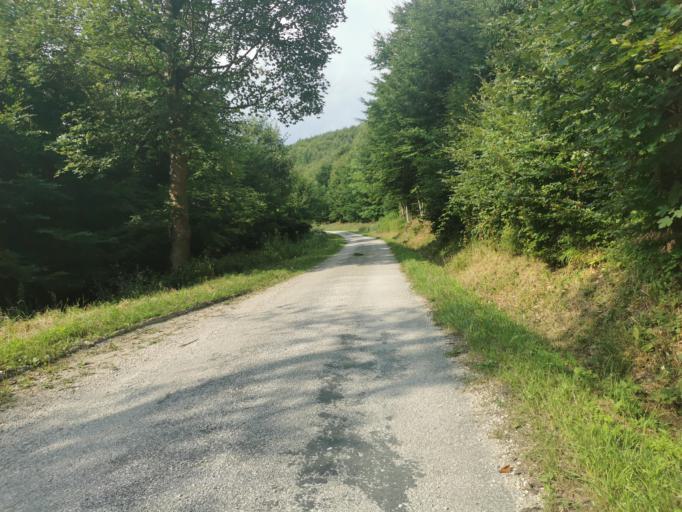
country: SK
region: Nitriansky
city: Stara Tura
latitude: 48.8206
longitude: 17.6315
